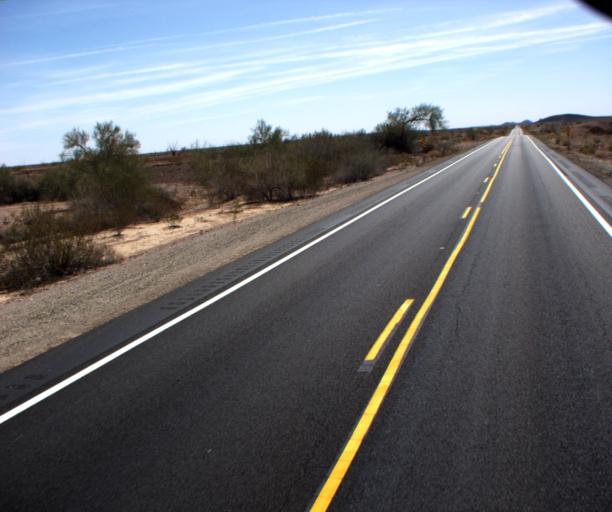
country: US
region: Arizona
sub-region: Yuma County
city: Wellton
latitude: 33.1309
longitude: -114.2890
